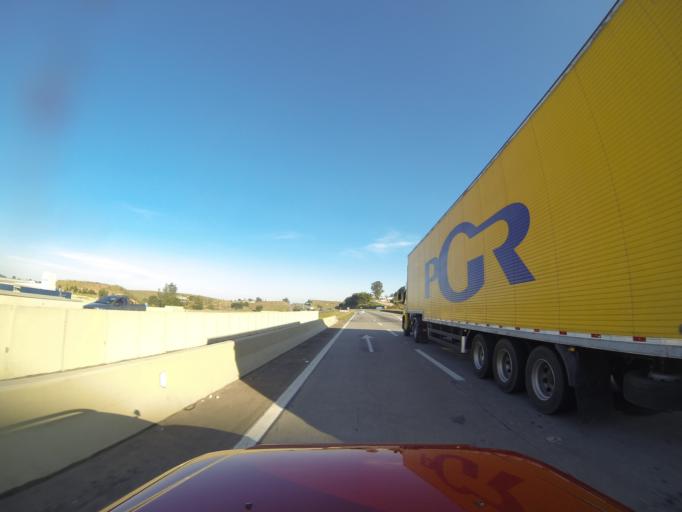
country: BR
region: Sao Paulo
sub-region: Jacarei
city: Jacarei
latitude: -23.2705
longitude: -46.0586
